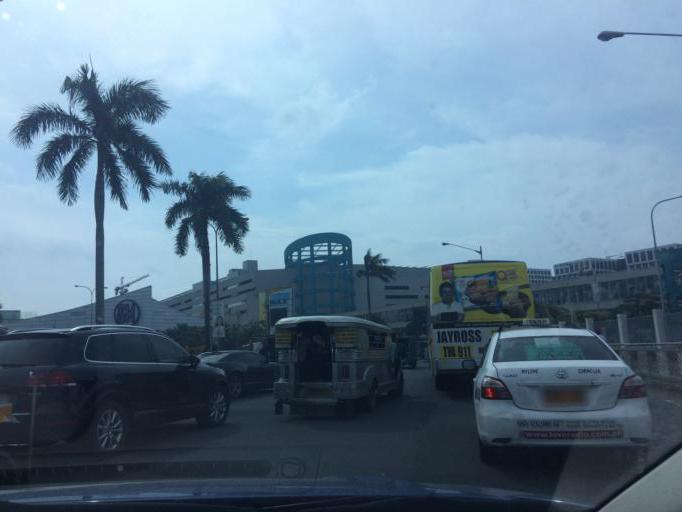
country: PH
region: Metro Manila
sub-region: Makati City
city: Makati City
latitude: 14.5360
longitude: 120.9847
